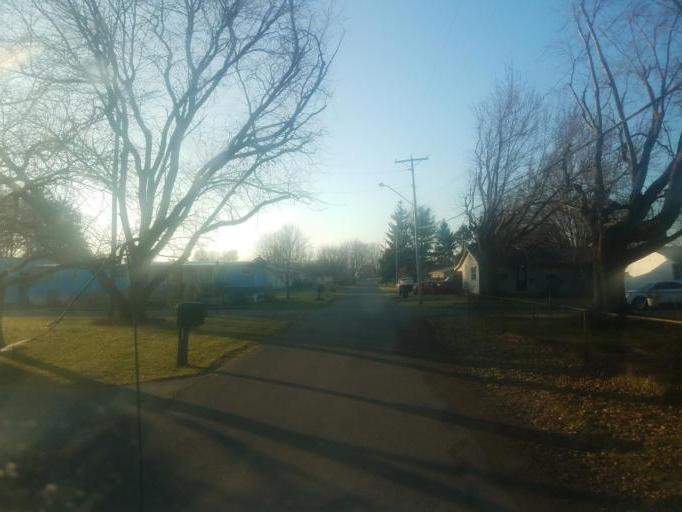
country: US
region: Ohio
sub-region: Crawford County
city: Bucyrus
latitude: 40.8215
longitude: -82.9687
